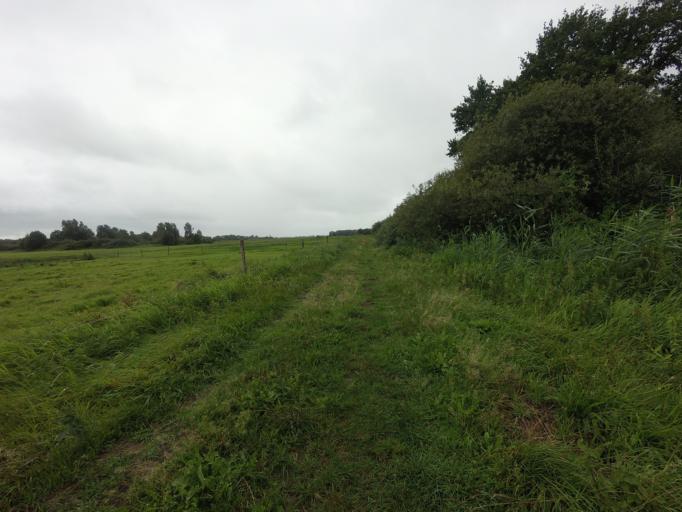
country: NL
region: Overijssel
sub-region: Gemeente Steenwijkerland
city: Blokzijl
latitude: 52.7647
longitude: 5.9779
